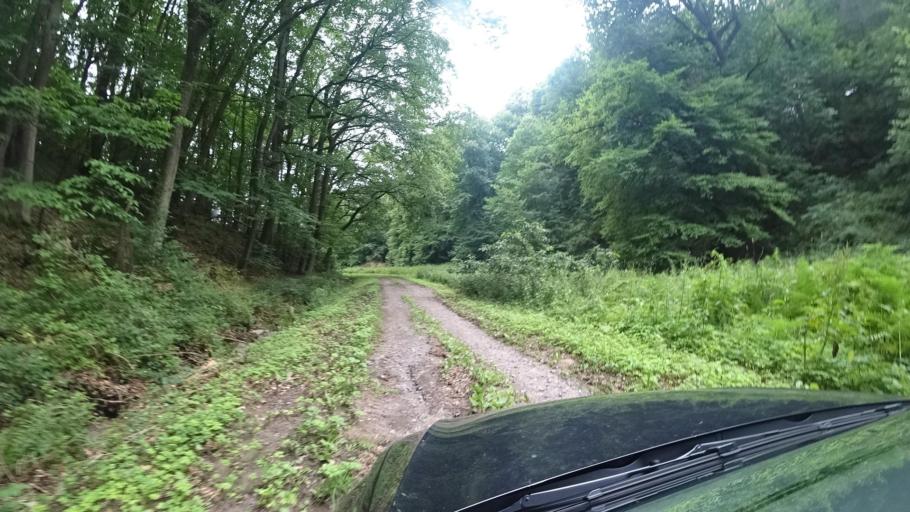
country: DE
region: Rheinland-Pfalz
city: Dorrenbach
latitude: 49.0909
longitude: 7.9770
